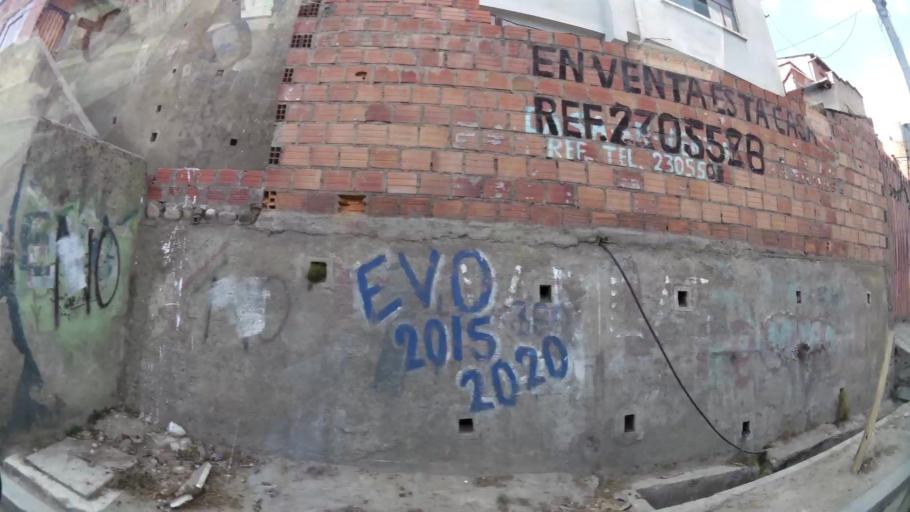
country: BO
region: La Paz
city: La Paz
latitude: -16.4856
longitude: -68.1407
